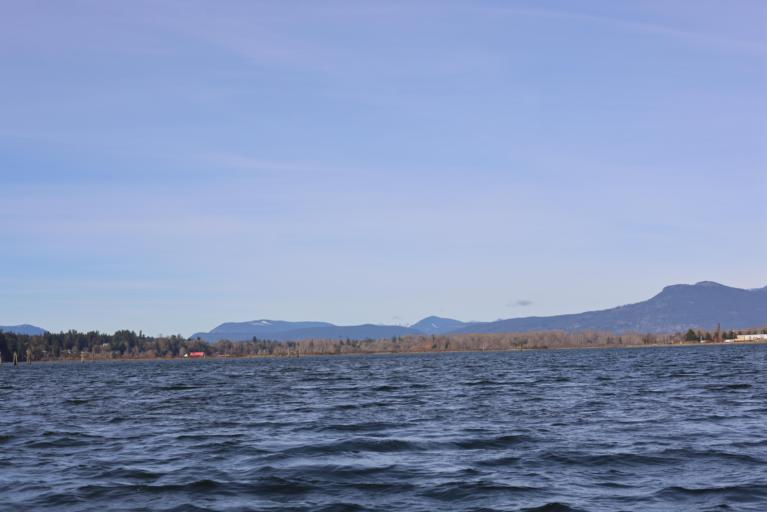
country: CA
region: British Columbia
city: Duncan
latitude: 48.7446
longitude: -123.6238
